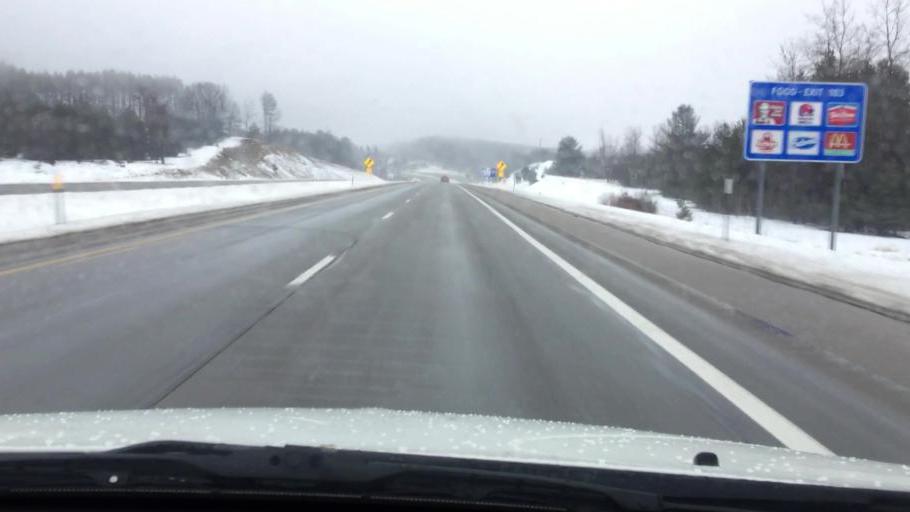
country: US
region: Michigan
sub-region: Wexford County
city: Cadillac
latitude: 44.3063
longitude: -85.3925
